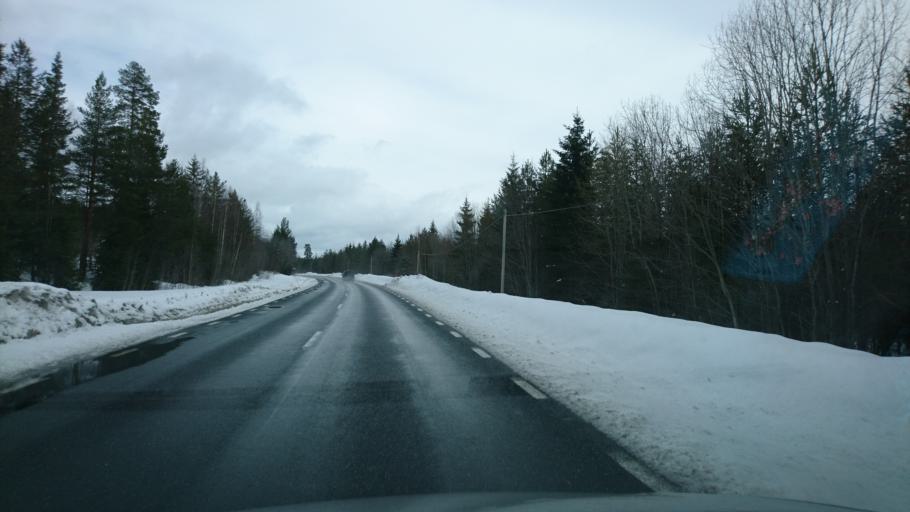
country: SE
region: Vaesternorrland
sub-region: Solleftea Kommun
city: Solleftea
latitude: 63.0491
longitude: 17.0528
